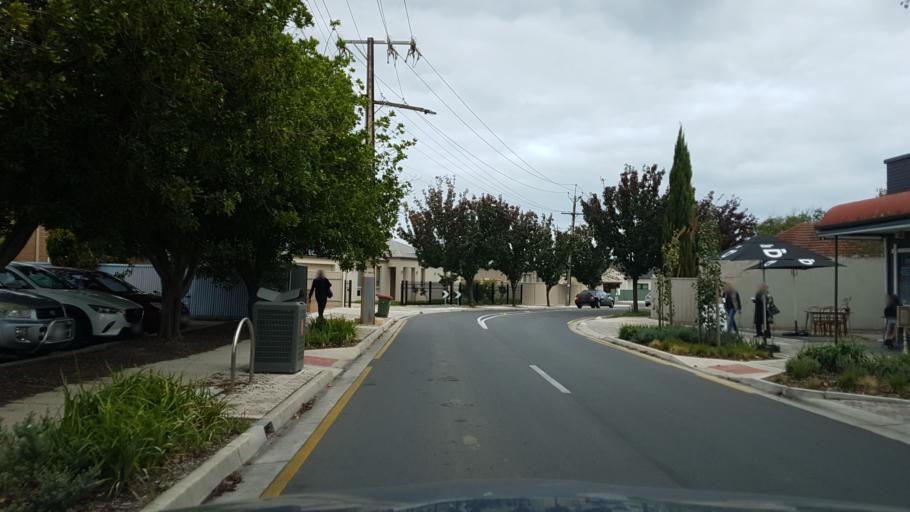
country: AU
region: South Australia
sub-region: City of West Torrens
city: Plympton
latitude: -34.9567
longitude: 138.5635
